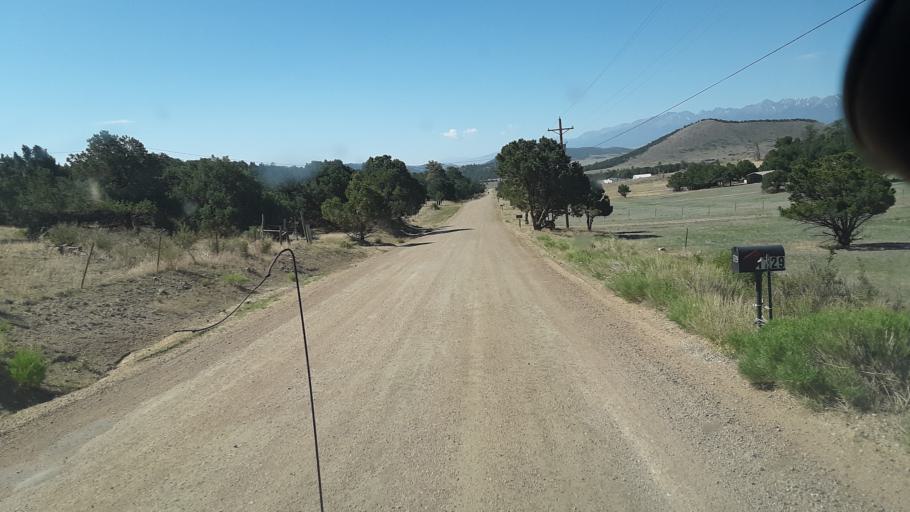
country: US
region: Colorado
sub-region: Custer County
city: Westcliffe
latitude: 38.3213
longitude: -105.4875
